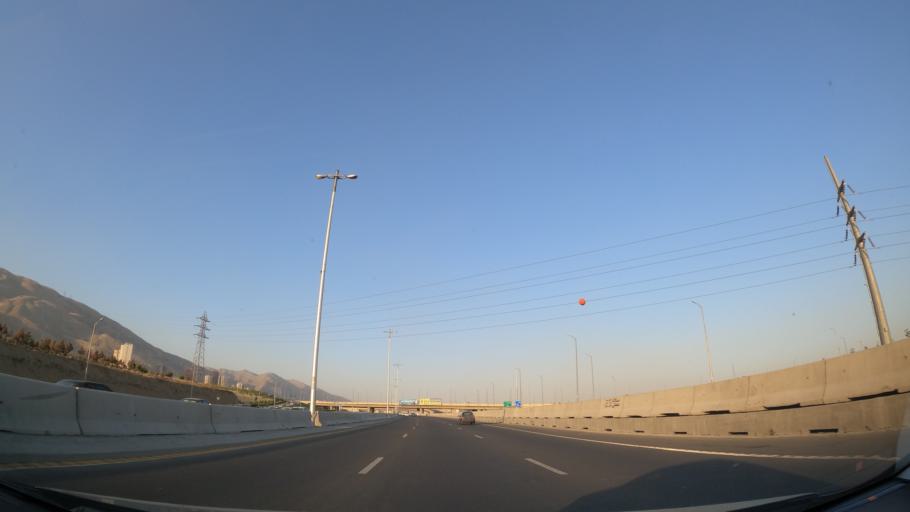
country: IR
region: Tehran
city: Shahr-e Qods
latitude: 35.7421
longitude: 51.1218
